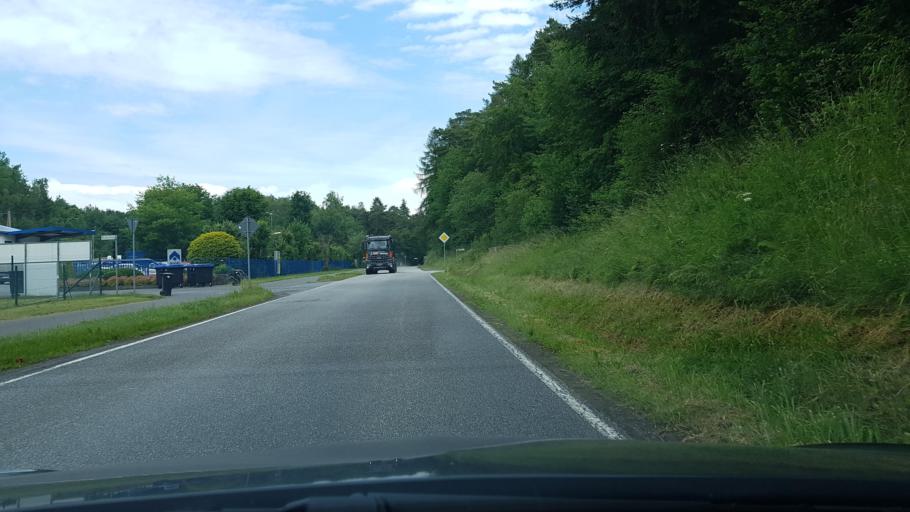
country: DE
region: Rheinland-Pfalz
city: Volkesfeld
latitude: 50.4135
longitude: 7.1537
